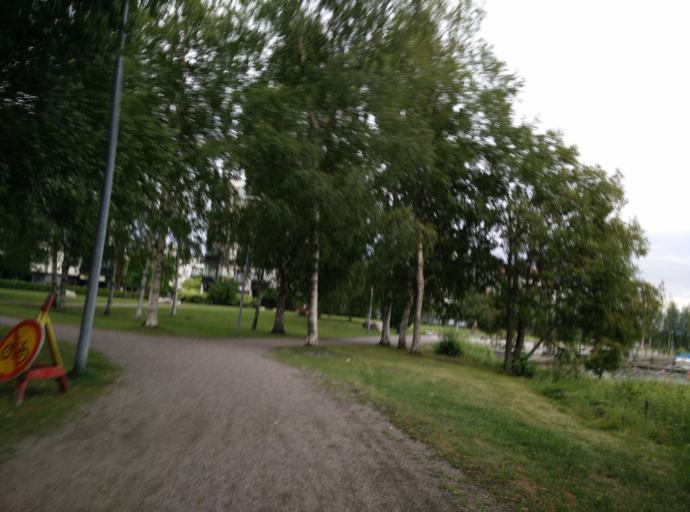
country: FI
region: Haeme
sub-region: Haemeenlinna
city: Haemeenlinna
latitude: 60.9956
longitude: 24.4765
